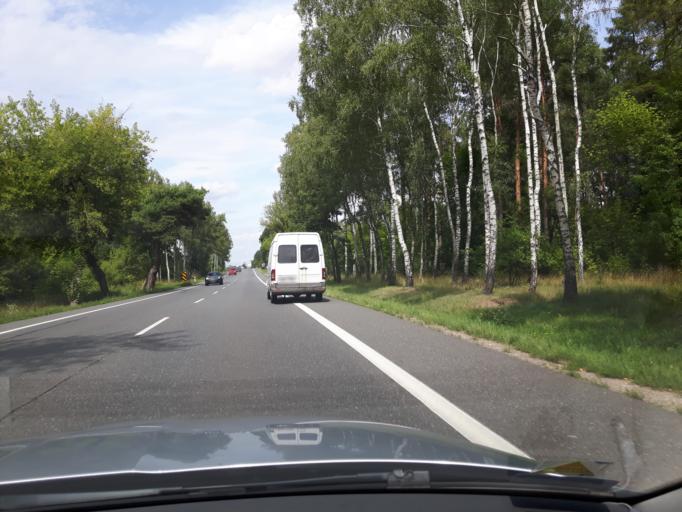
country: PL
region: Masovian Voivodeship
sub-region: Powiat mlawski
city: Strzegowo
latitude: 52.9167
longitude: 20.2864
